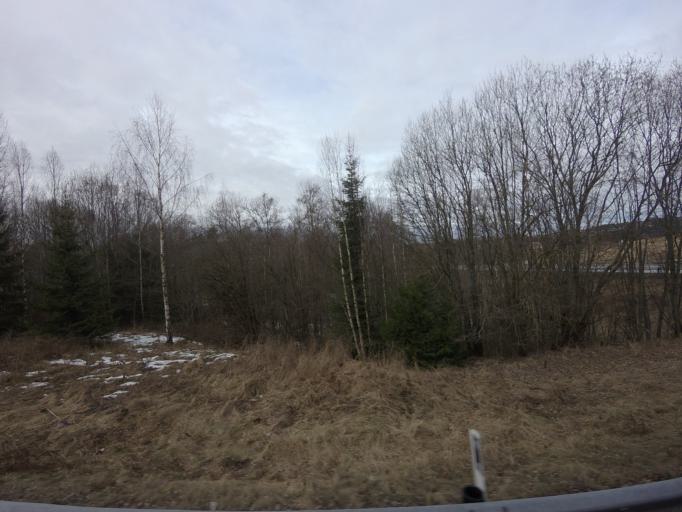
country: NO
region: Akershus
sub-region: Fet
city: Fetsund
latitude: 59.9219
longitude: 11.1837
